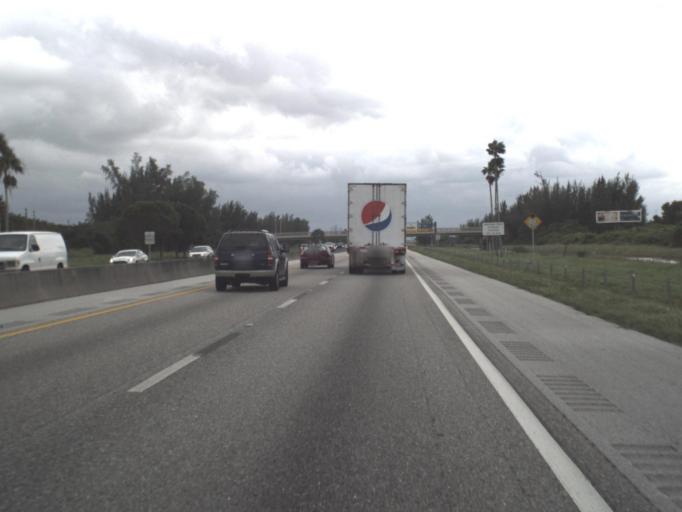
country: US
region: Florida
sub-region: Palm Beach County
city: Greenacres City
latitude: 26.5777
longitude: -80.1733
